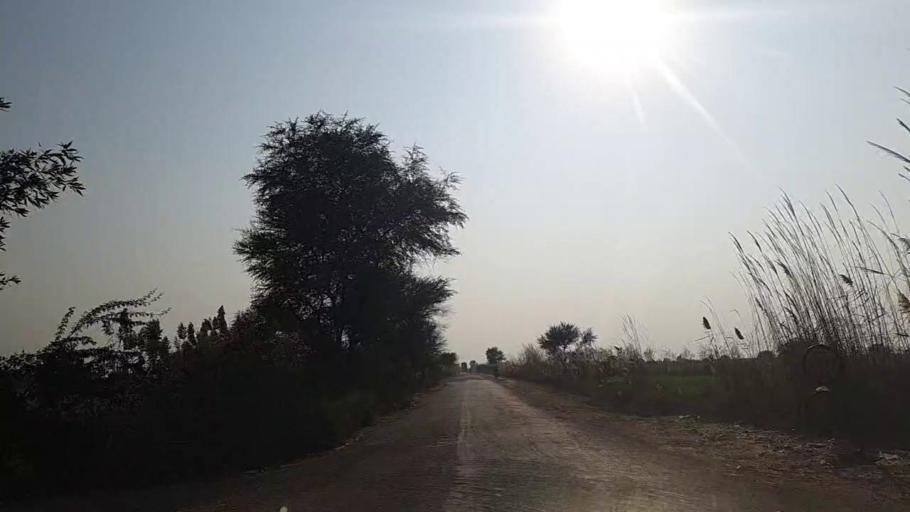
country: PK
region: Sindh
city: Jam Sahib
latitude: 26.2766
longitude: 68.6160
